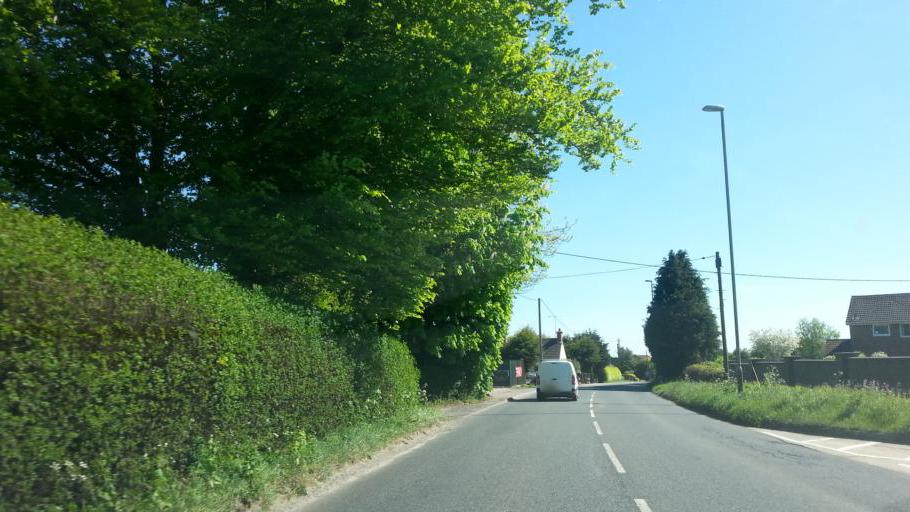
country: GB
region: England
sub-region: Dorset
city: Shaftesbury
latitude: 51.0192
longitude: -2.1886
